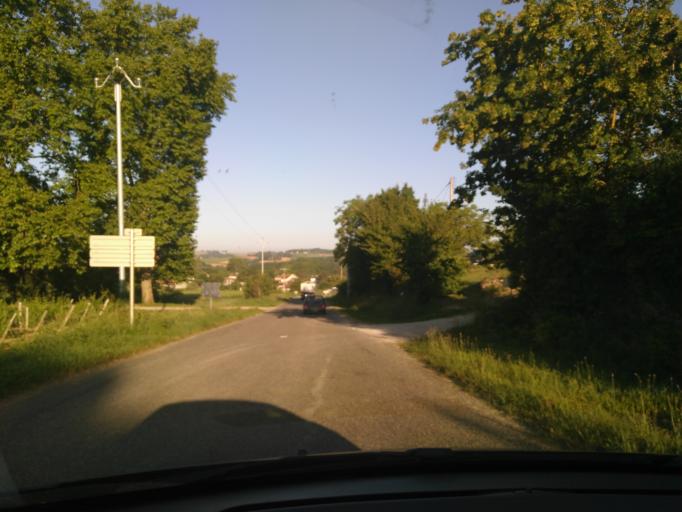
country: FR
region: Midi-Pyrenees
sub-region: Departement du Gers
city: Gondrin
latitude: 43.9037
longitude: 0.3041
